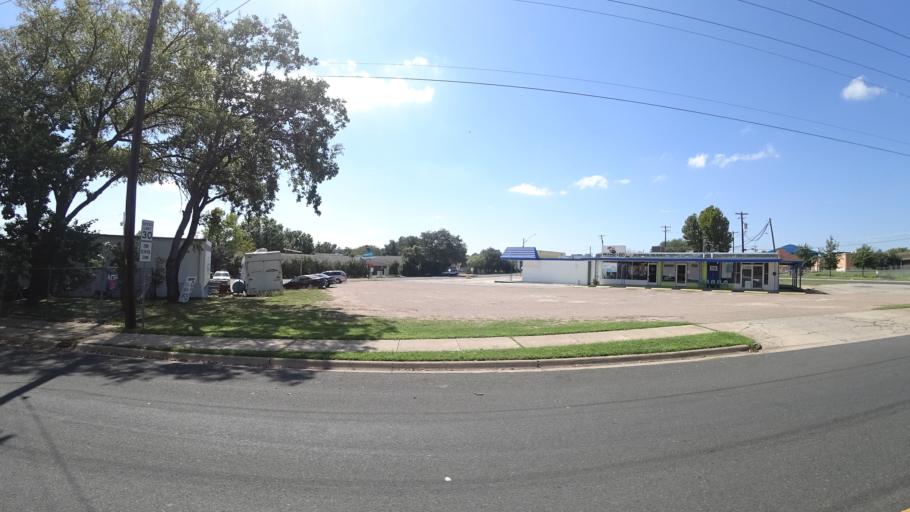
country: US
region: Texas
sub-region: Travis County
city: Austin
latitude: 30.3146
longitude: -97.6894
